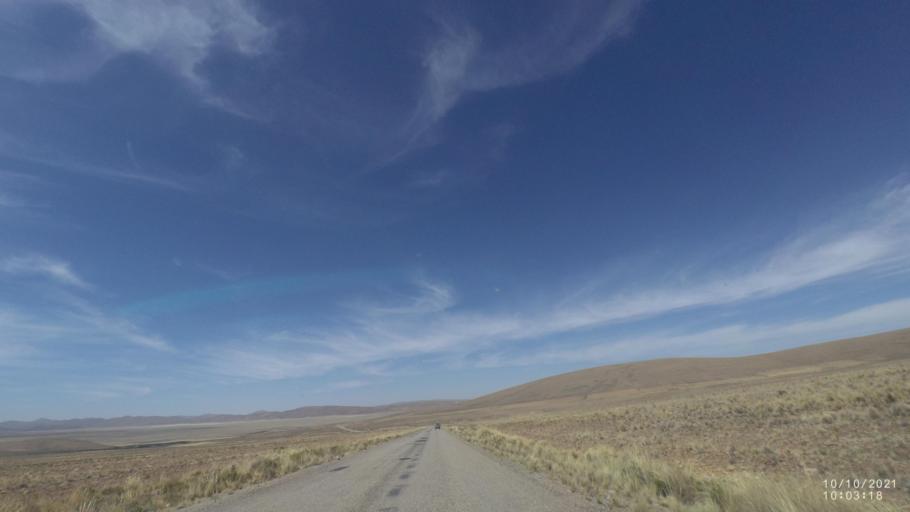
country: BO
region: La Paz
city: Eucaliptus
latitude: -17.3676
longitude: -67.4393
